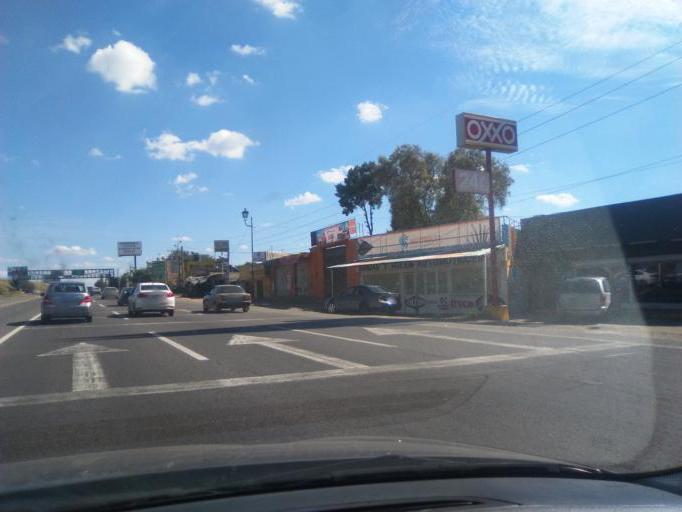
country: MX
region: Guanajuato
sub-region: Silao de la Victoria
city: El Refugio de los Sauces
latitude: 21.0259
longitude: -101.5408
